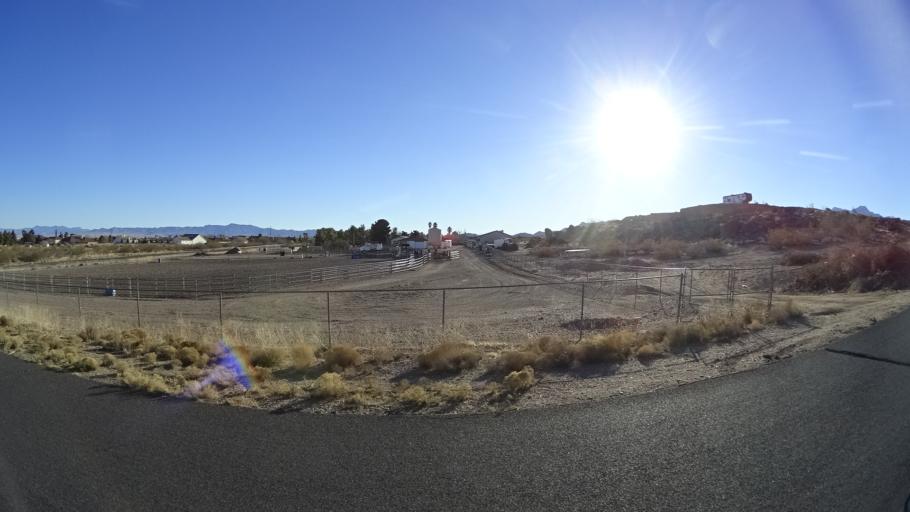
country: US
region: Arizona
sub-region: Mohave County
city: Kingman
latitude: 35.2059
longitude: -114.0028
